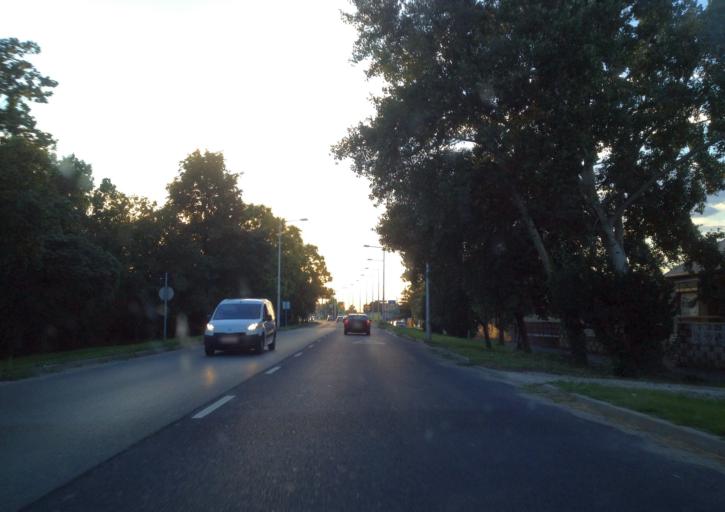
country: HU
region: Gyor-Moson-Sopron
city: Mosonmagyarovar
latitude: 47.8747
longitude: 17.2646
